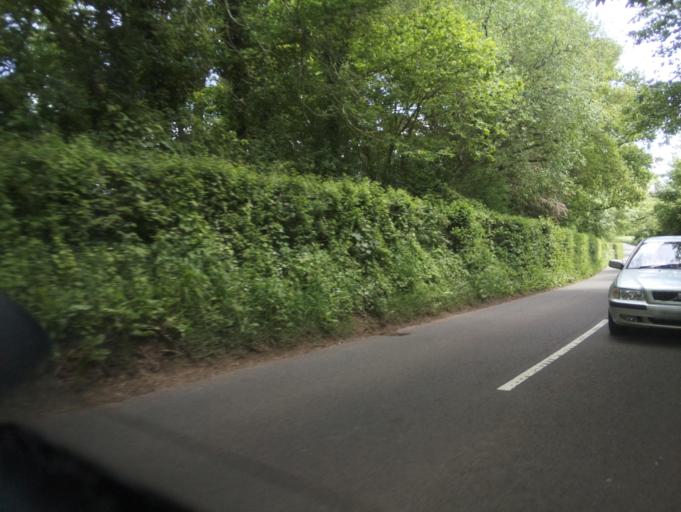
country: GB
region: England
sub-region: Herefordshire
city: Llanrothal
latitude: 51.8616
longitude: -2.8130
